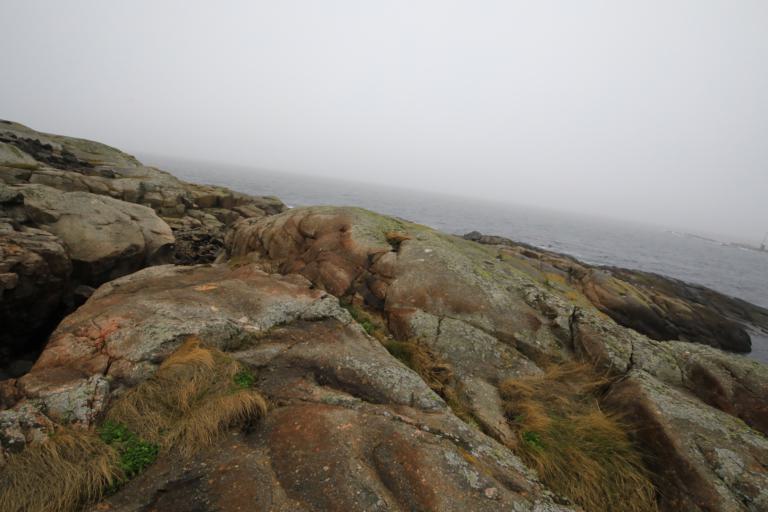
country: SE
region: Vaestra Goetaland
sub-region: Ockero Kommun
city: Hono
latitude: 57.6347
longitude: 11.5961
